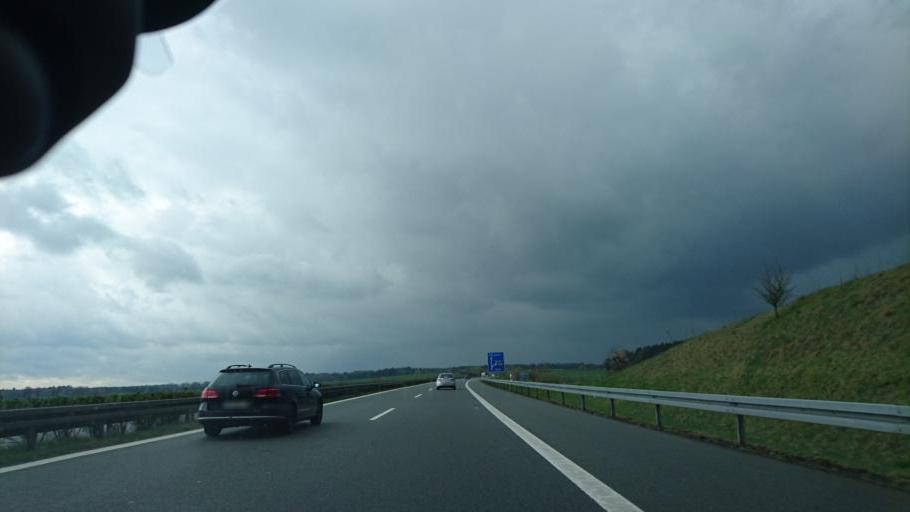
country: DE
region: Mecklenburg-Vorpommern
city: Tessin
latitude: 54.0152
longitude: 12.5542
